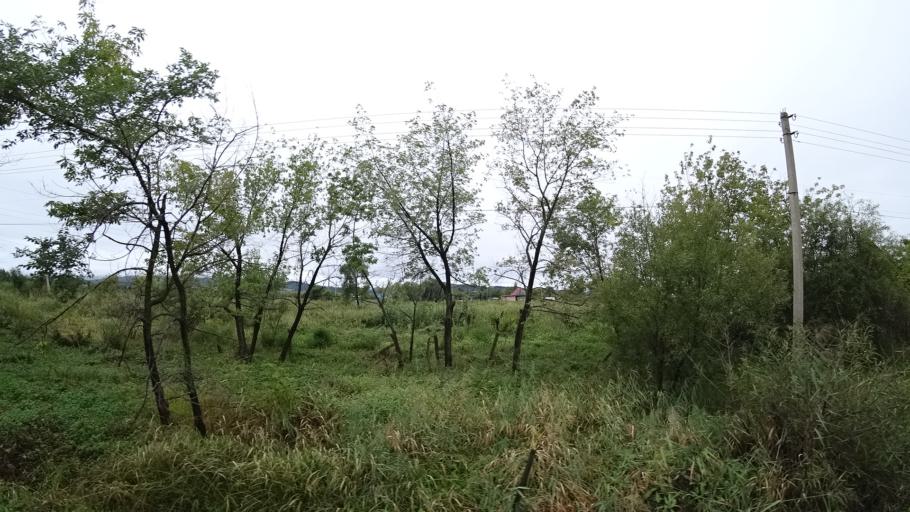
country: RU
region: Primorskiy
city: Monastyrishche
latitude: 44.1962
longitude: 132.4666
